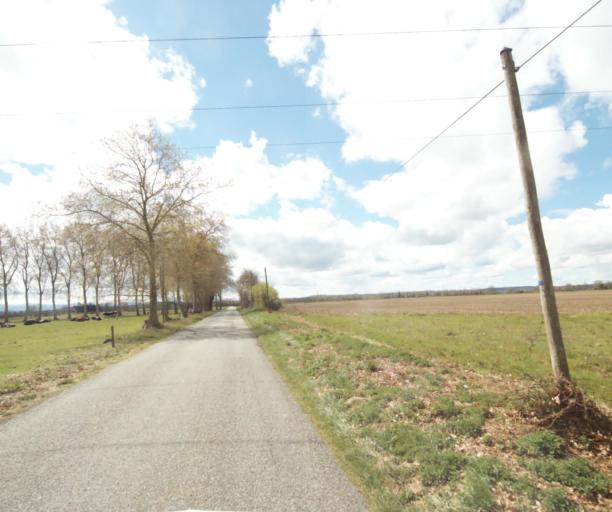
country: FR
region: Midi-Pyrenees
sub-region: Departement de l'Ariege
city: Saverdun
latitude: 43.2574
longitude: 1.6028
